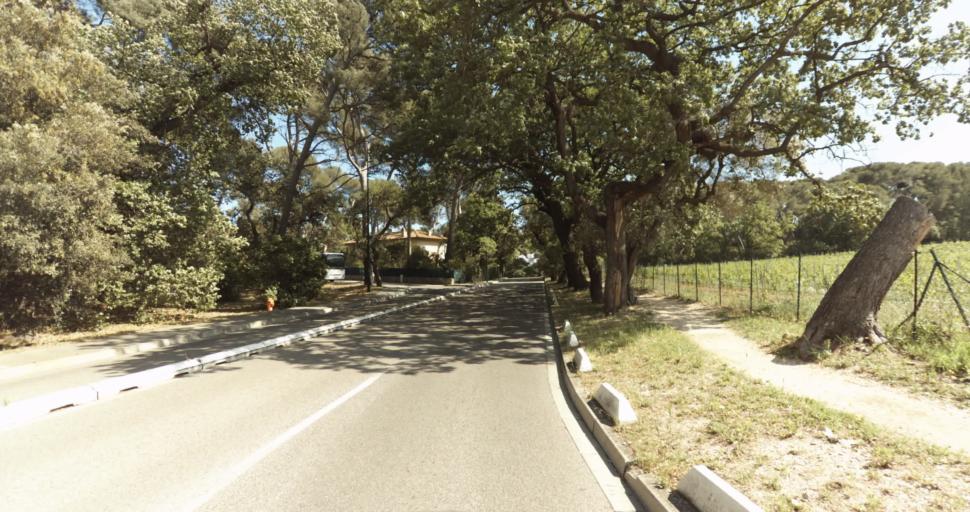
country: FR
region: Provence-Alpes-Cote d'Azur
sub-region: Departement du Var
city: Hyeres
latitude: 43.0977
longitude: 6.1220
